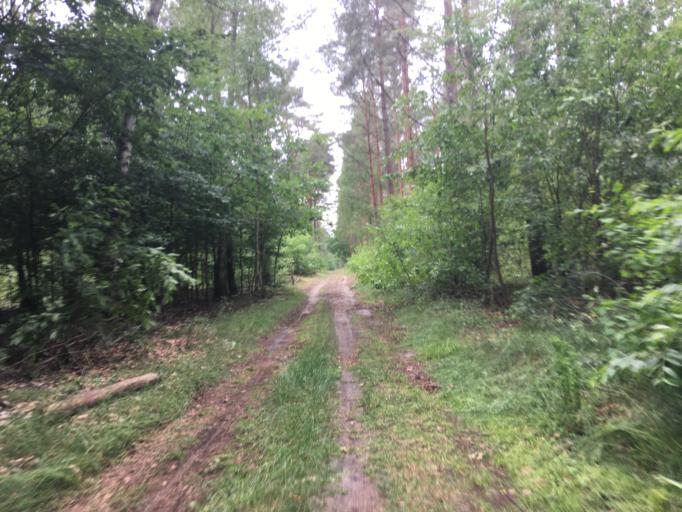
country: DE
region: Berlin
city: Rahnsdorf
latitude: 52.4204
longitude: 13.7018
